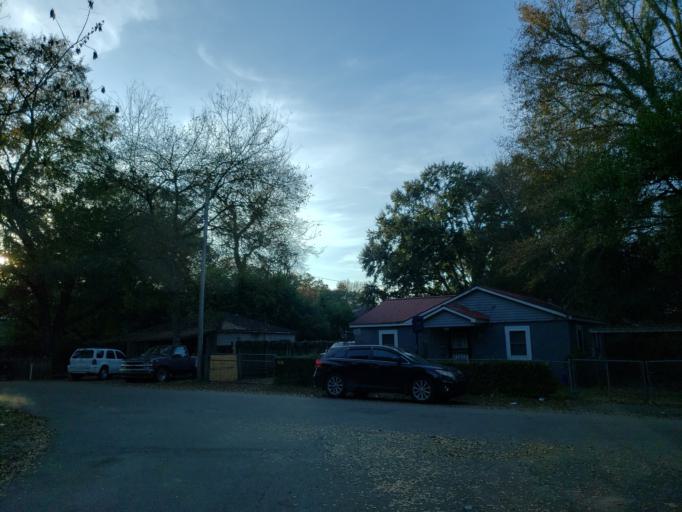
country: US
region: Mississippi
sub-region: Forrest County
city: Hattiesburg
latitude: 31.3365
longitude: -89.2982
